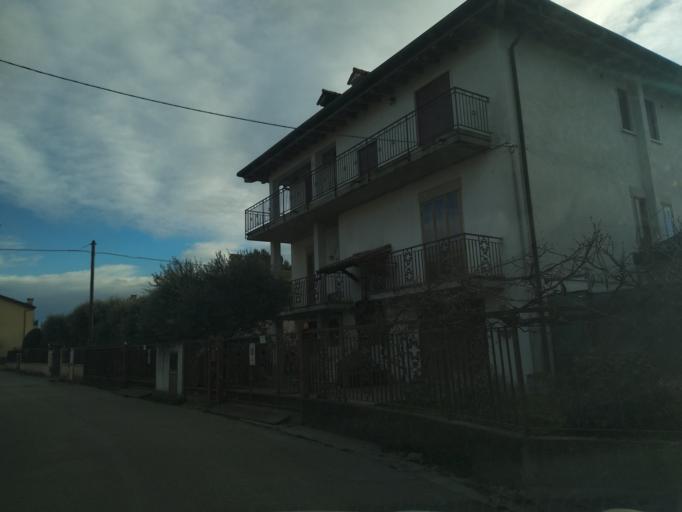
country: IT
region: Veneto
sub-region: Provincia di Vicenza
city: Lisiera
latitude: 45.5770
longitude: 11.5906
